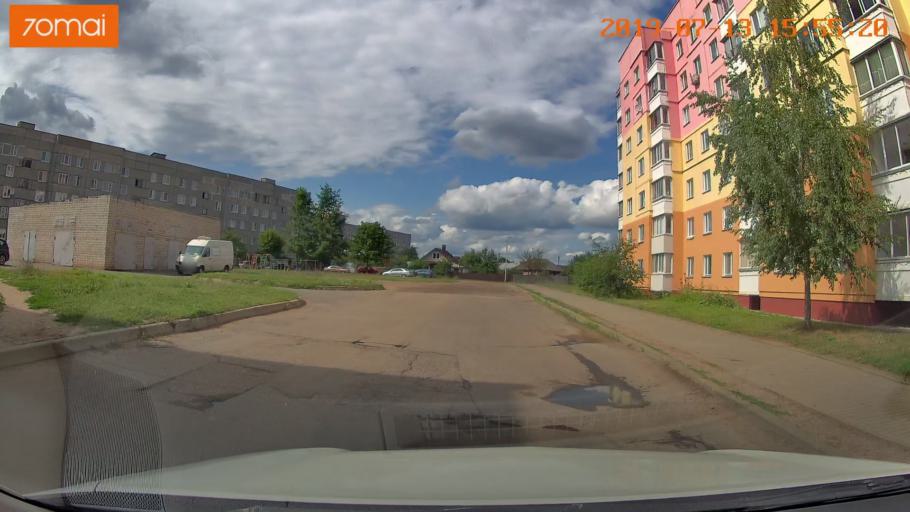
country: BY
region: Mogilev
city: Babruysk
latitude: 53.1415
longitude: 29.1976
